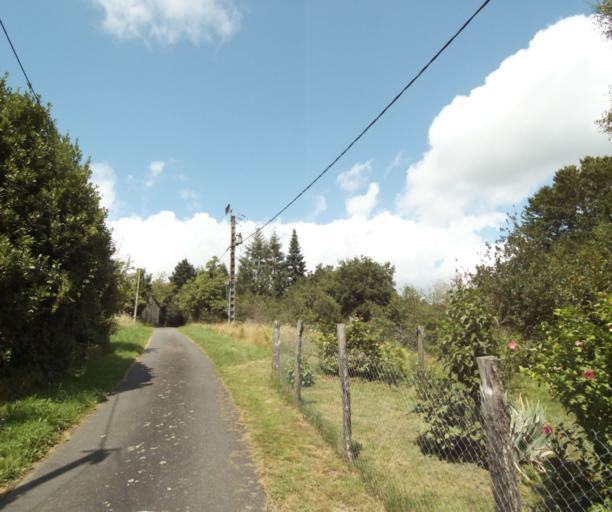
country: FR
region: Limousin
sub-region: Departement de la Correze
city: Sainte-Fortunade
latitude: 45.1966
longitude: 1.8424
